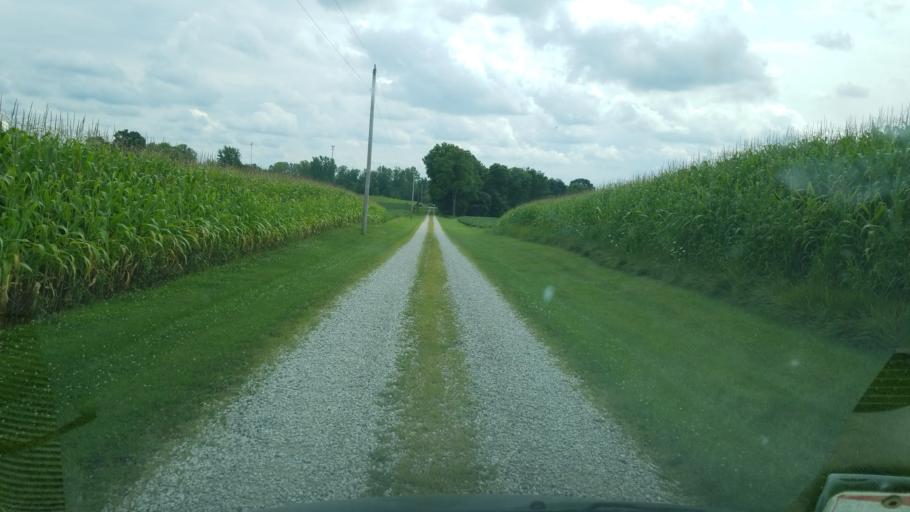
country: US
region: Ohio
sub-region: Morrow County
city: Mount Gilead
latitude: 40.5080
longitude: -82.7224
